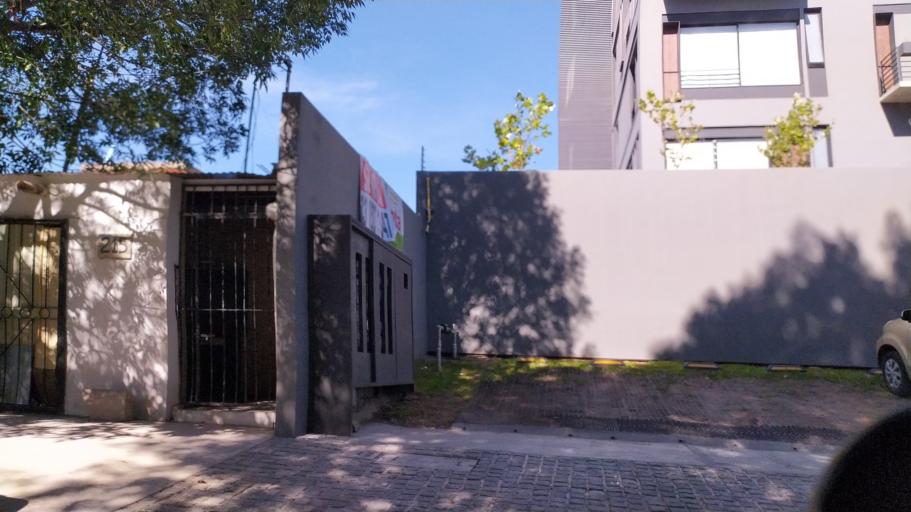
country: MX
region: Jalisco
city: Zapopan2
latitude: 20.6848
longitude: -103.4538
